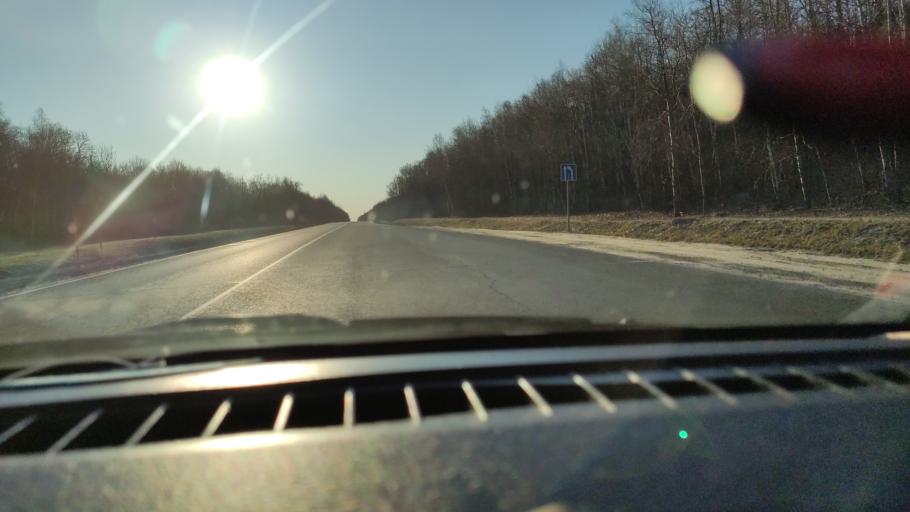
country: RU
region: Saratov
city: Vol'sk
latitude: 52.1120
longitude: 47.3268
